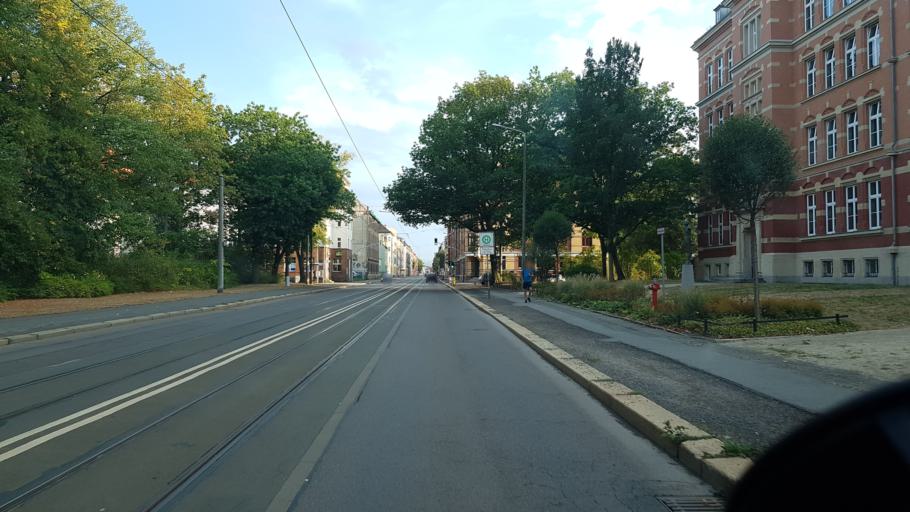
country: DE
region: Saxony
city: Zwickau
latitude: 50.7350
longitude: 12.4906
